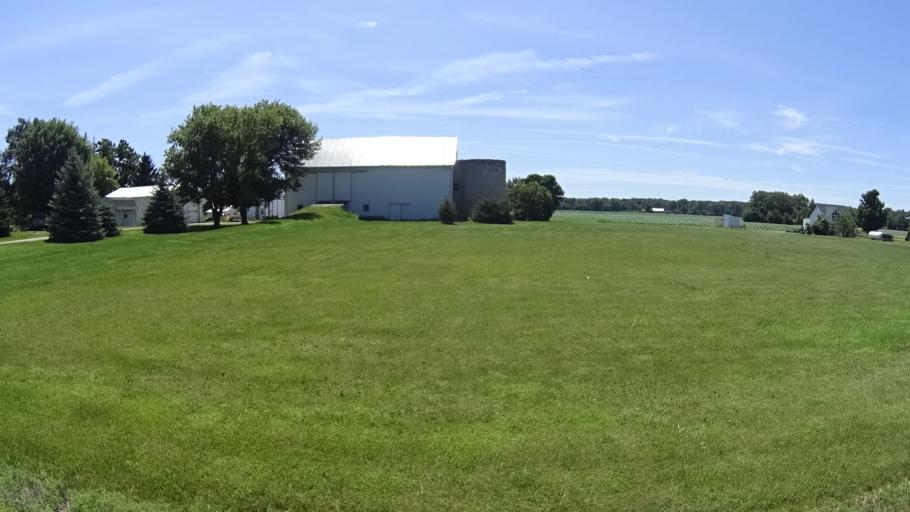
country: US
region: Ohio
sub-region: Erie County
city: Sandusky
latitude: 41.4363
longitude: -82.8270
